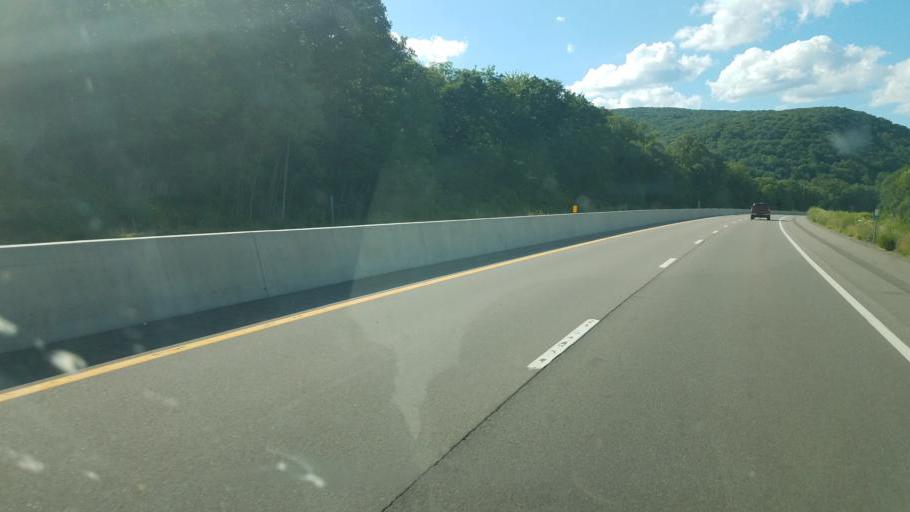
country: US
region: New York
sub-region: Cattaraugus County
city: Salamanca
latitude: 42.1009
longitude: -78.6604
